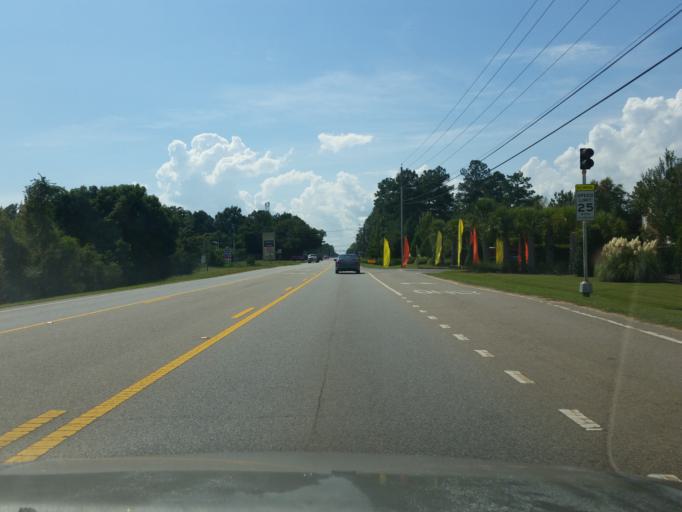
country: US
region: Alabama
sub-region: Baldwin County
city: Spanish Fort
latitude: 30.6768
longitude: -87.8445
